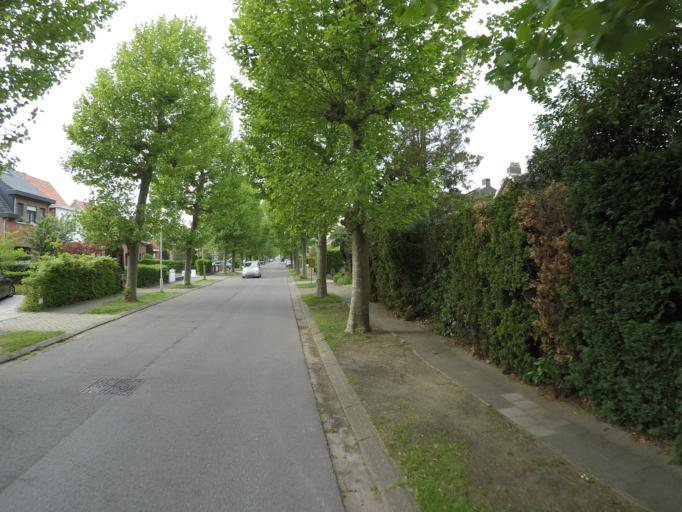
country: BE
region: Flanders
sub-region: Provincie Antwerpen
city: Kapellen
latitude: 51.3086
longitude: 4.4262
